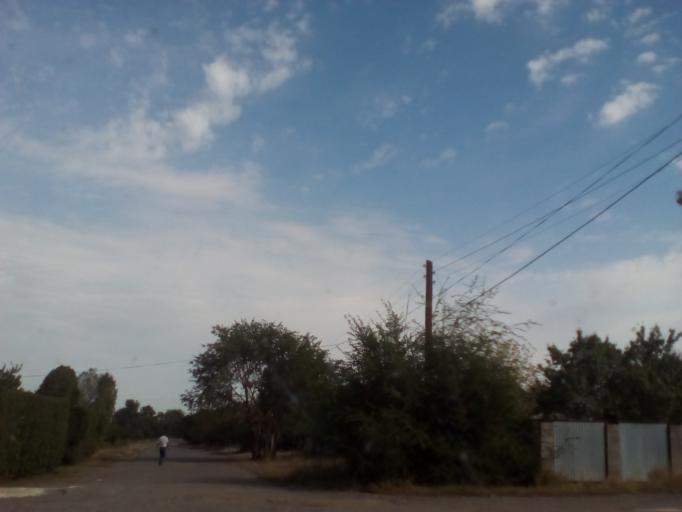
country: KZ
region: Almaty Oblysy
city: Burunday
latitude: 43.1666
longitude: 76.4051
